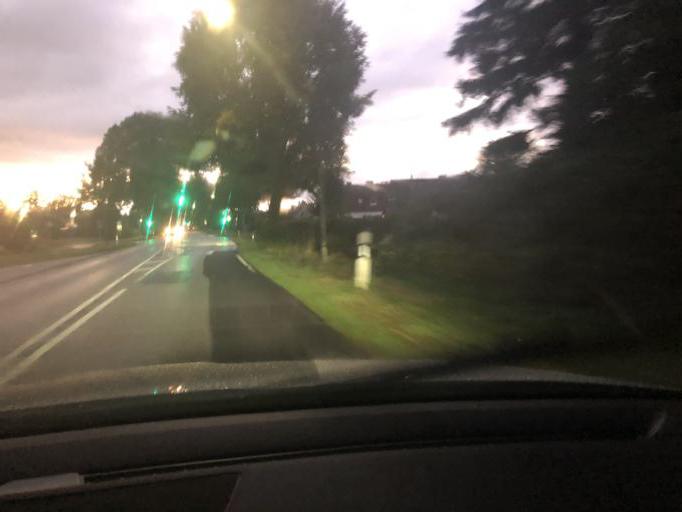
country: DE
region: Schleswig-Holstein
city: Gross Gronau
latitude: 53.8149
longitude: 10.7379
